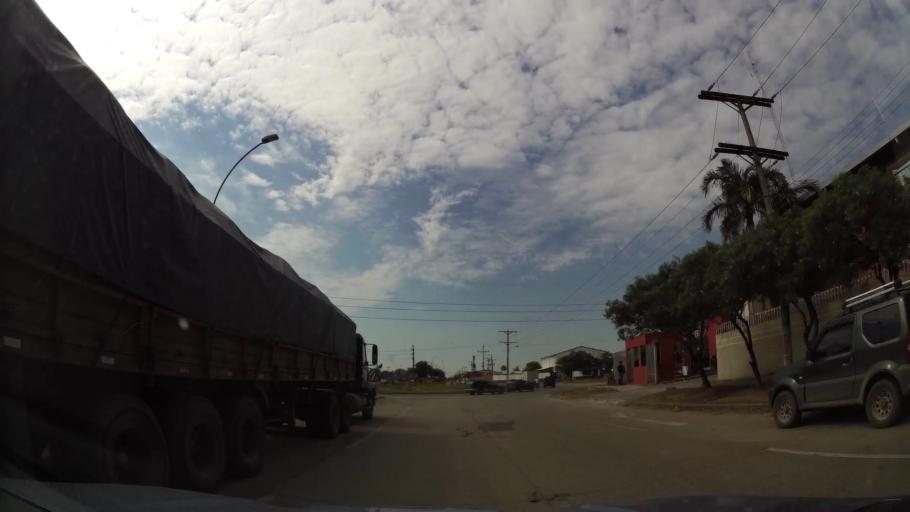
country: BO
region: Santa Cruz
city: Santa Cruz de la Sierra
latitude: -17.7424
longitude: -63.1667
